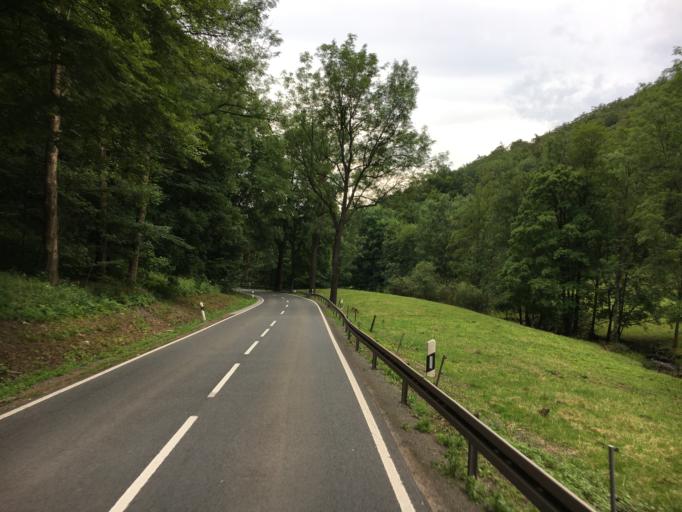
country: DE
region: Thuringia
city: Brotterode
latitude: 50.8097
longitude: 10.4293
